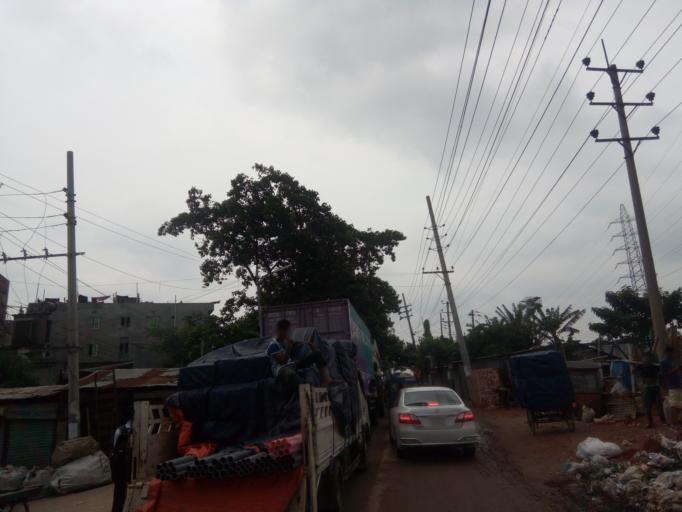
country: BD
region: Dhaka
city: Azimpur
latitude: 23.7148
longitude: 90.3806
